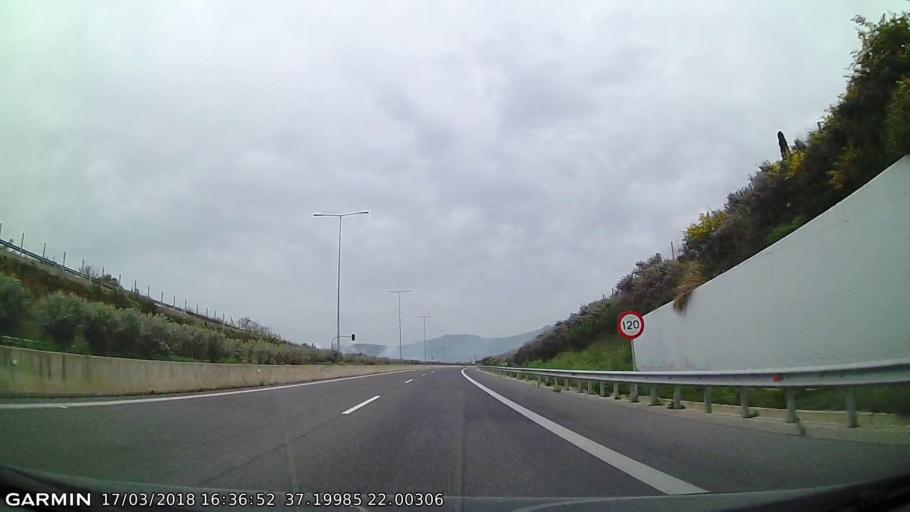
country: GR
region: Peloponnese
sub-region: Nomos Messinias
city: Meligalas
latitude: 37.2006
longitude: 22.0025
